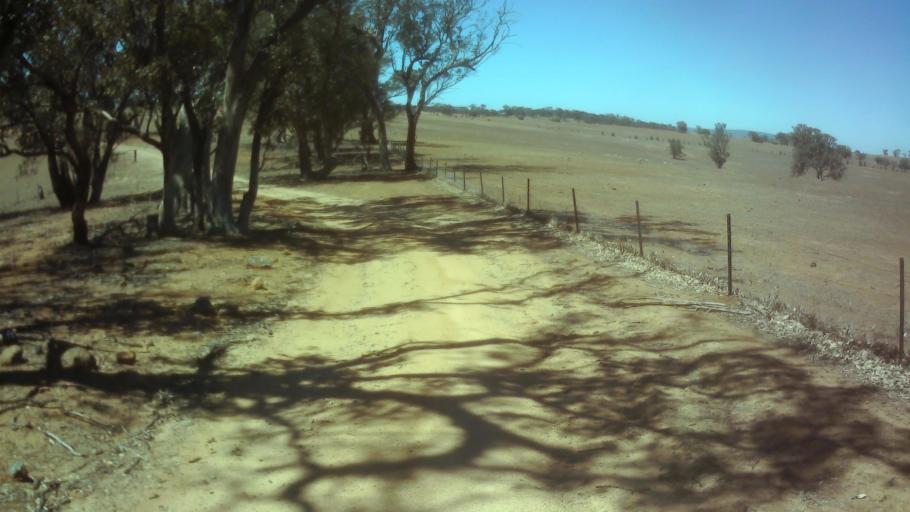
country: AU
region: New South Wales
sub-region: Cowra
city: Cowra
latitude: -33.8977
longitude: 148.5063
